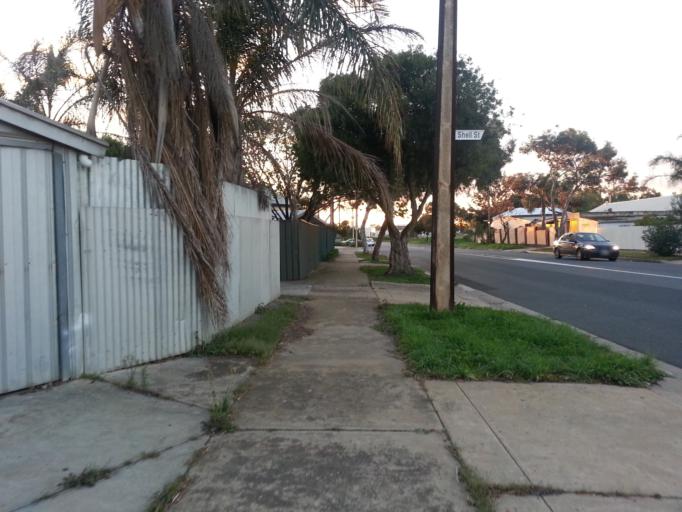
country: AU
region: South Australia
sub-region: Port Adelaide Enfield
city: Alberton
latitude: -34.8481
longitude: 138.5221
